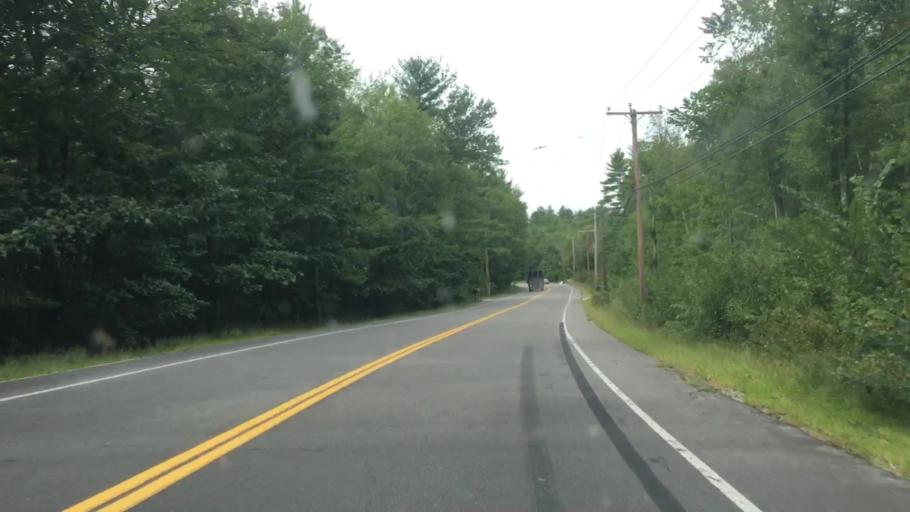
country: US
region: New Hampshire
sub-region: Strafford County
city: Madbury
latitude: 43.2035
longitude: -70.9678
